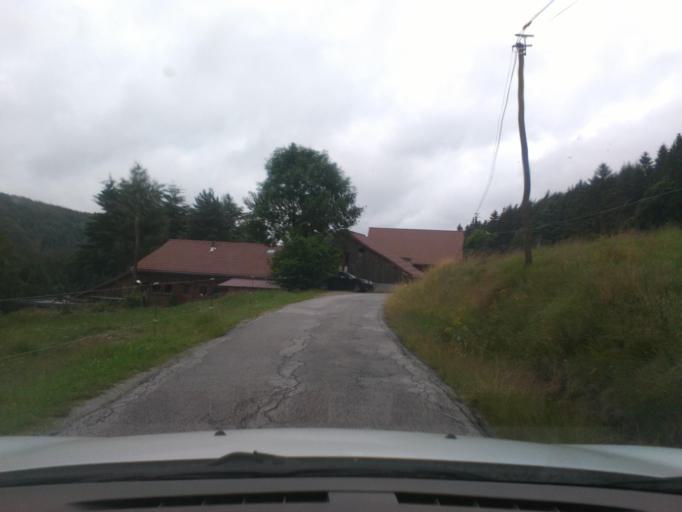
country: FR
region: Lorraine
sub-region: Departement des Vosges
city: Gerardmer
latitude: 48.0906
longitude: 6.8459
